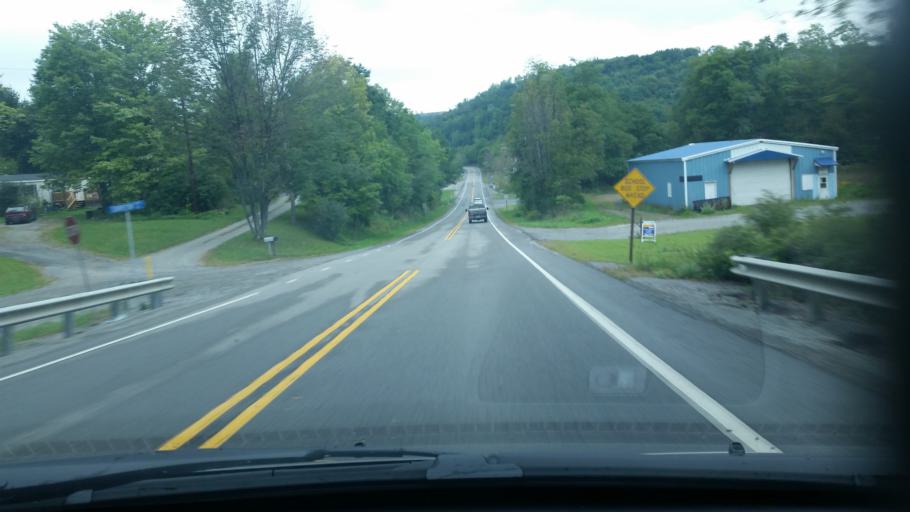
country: US
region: Pennsylvania
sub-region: Clearfield County
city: Shiloh
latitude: 41.0718
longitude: -78.3252
